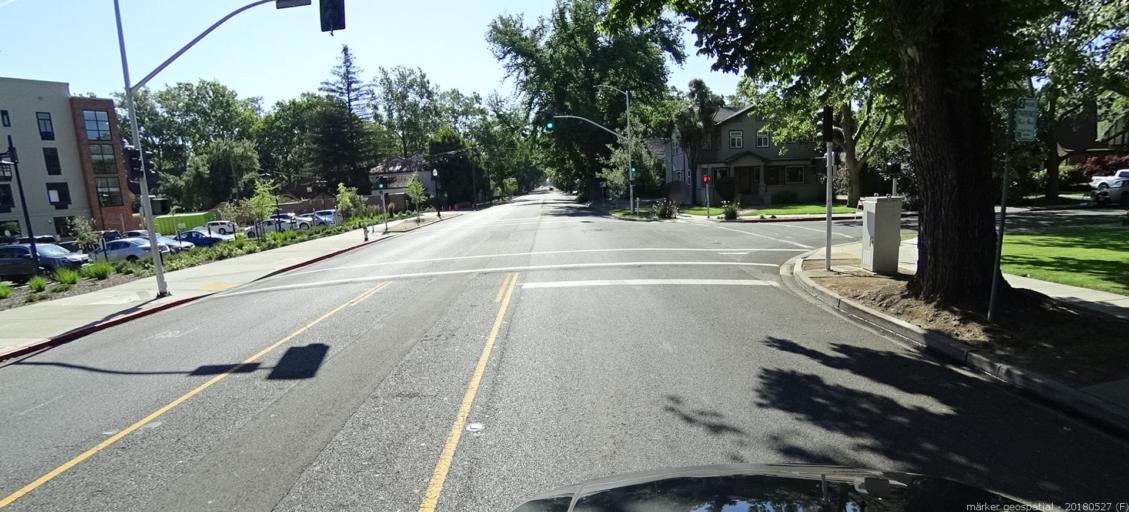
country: US
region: California
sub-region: Sacramento County
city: Sacramento
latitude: 38.5695
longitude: -121.4531
